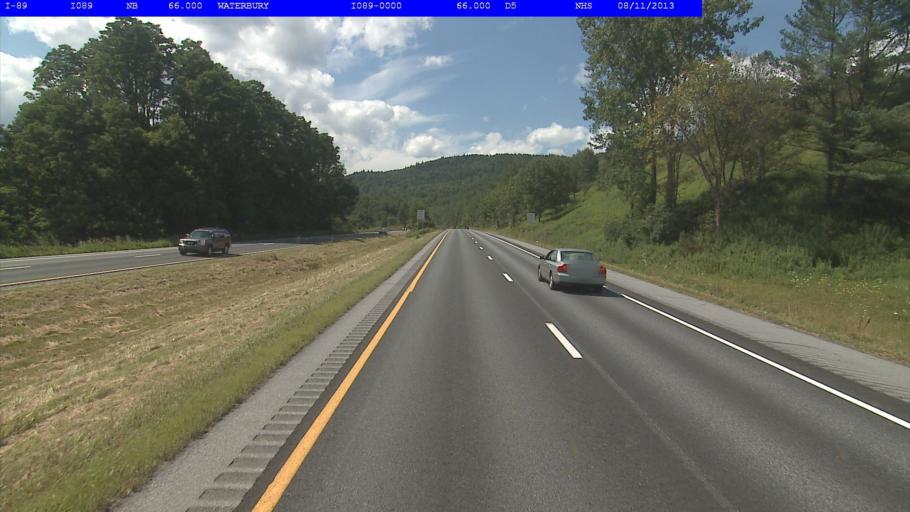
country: US
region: Vermont
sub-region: Washington County
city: Waterbury
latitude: 44.3575
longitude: -72.7917
